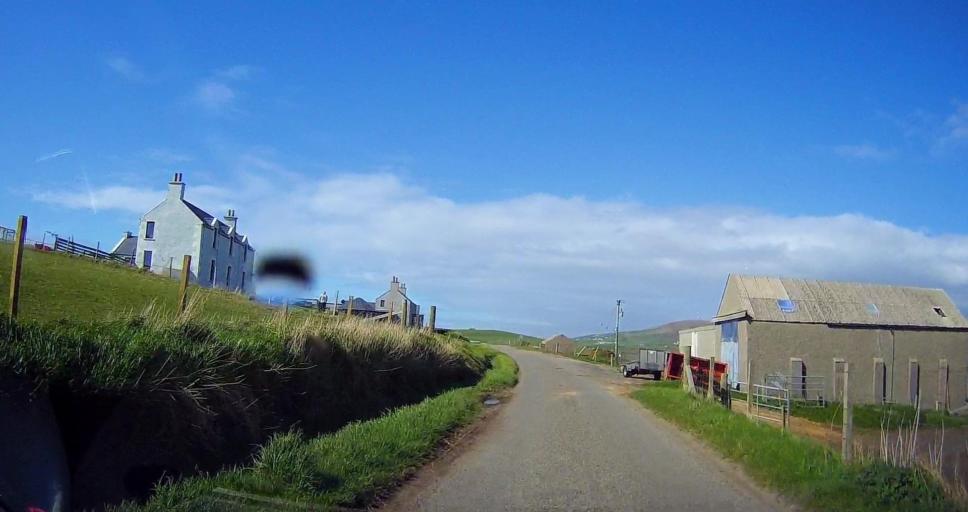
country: GB
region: Scotland
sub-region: Shetland Islands
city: Sandwick
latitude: 59.9081
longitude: -1.3343
